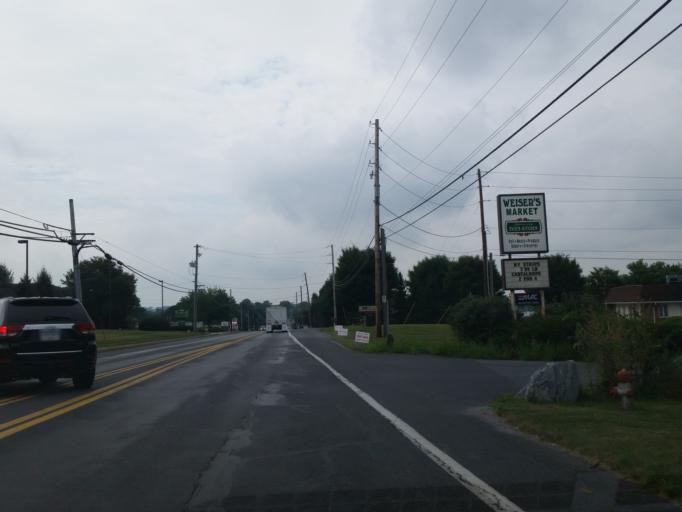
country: US
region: Pennsylvania
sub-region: Lancaster County
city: Lititz
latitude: 40.1742
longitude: -76.3087
